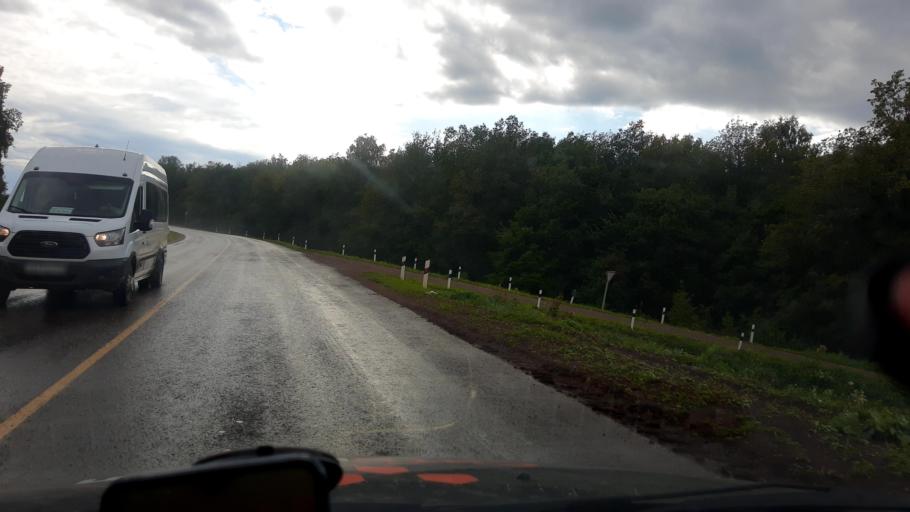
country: RU
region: Bashkortostan
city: Karmaskaly
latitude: 53.9233
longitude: 56.3524
